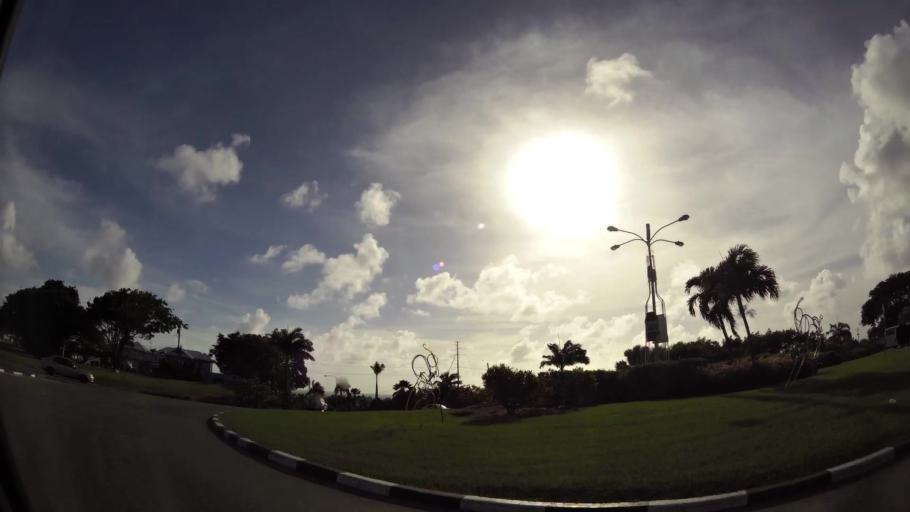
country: BB
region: Christ Church
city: Oistins
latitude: 13.0773
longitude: -59.5682
